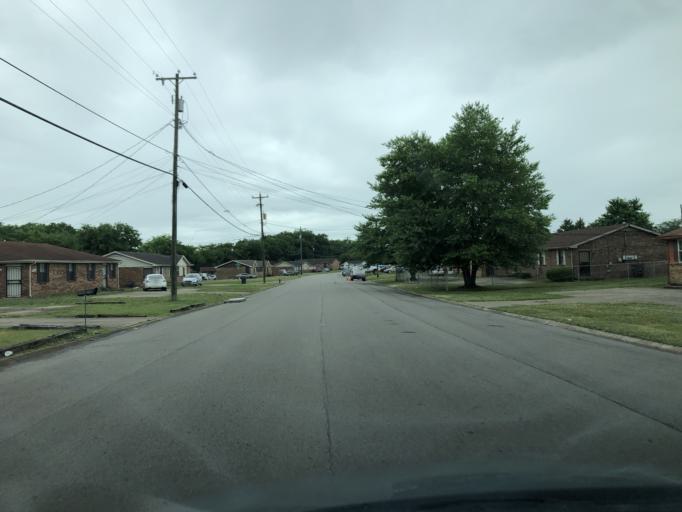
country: US
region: Tennessee
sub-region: Davidson County
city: Nashville
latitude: 36.2474
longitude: -86.7736
